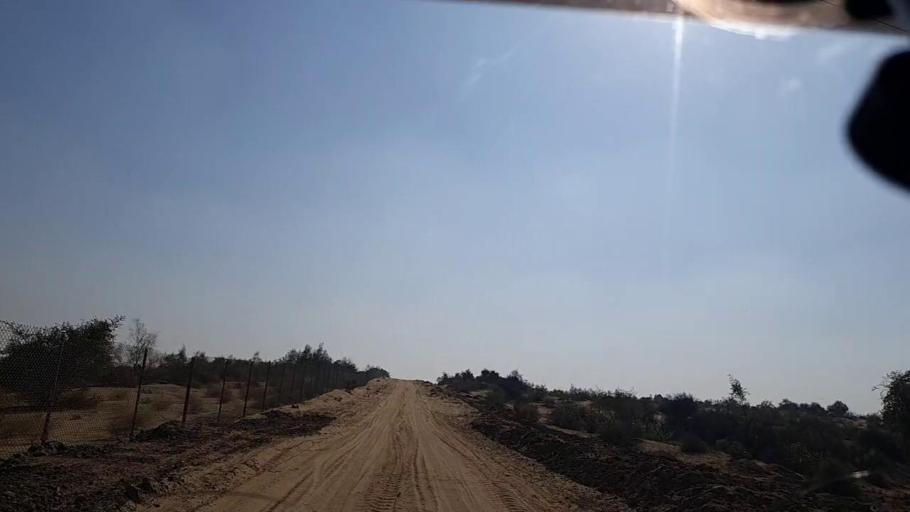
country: PK
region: Sindh
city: Khanpur
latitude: 27.5643
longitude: 69.3888
